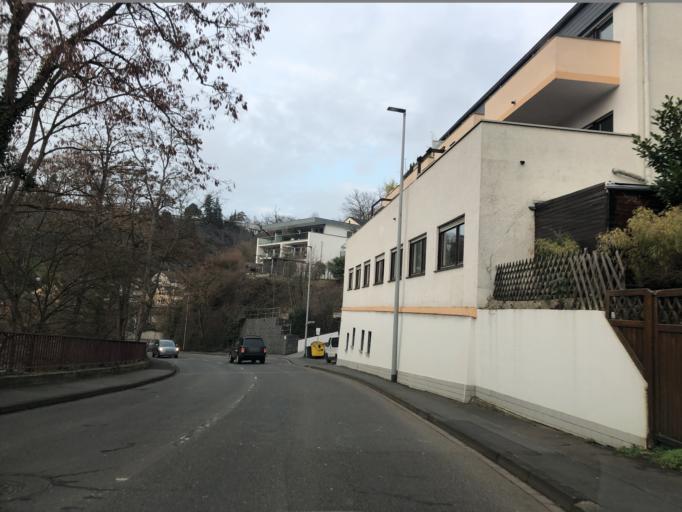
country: DE
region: Rheinland-Pfalz
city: Lahnstein
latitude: 50.3012
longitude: 7.6149
